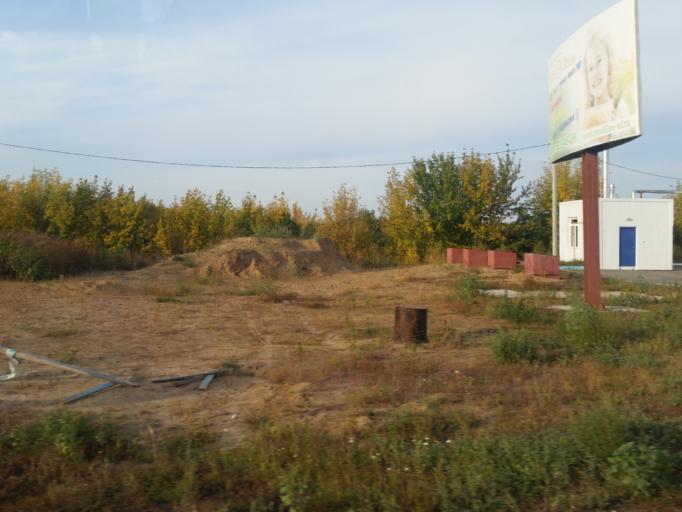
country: RU
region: Ulyanovsk
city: Cherdakly
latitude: 54.3552
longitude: 48.8744
